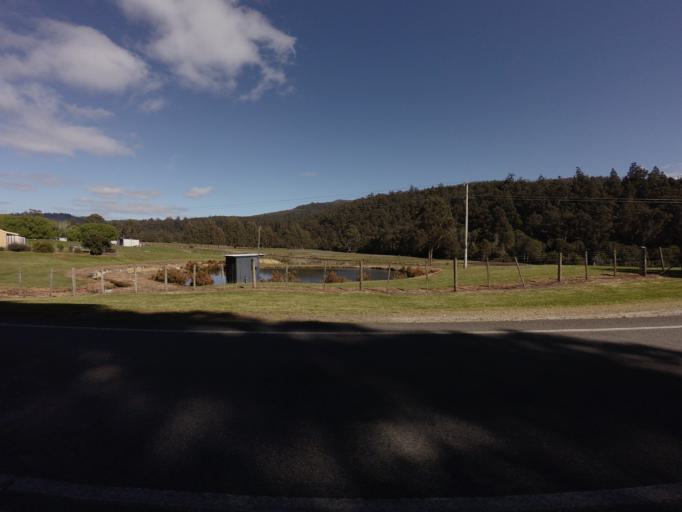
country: AU
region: Tasmania
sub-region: Derwent Valley
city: New Norfolk
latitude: -42.7224
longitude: 146.6793
